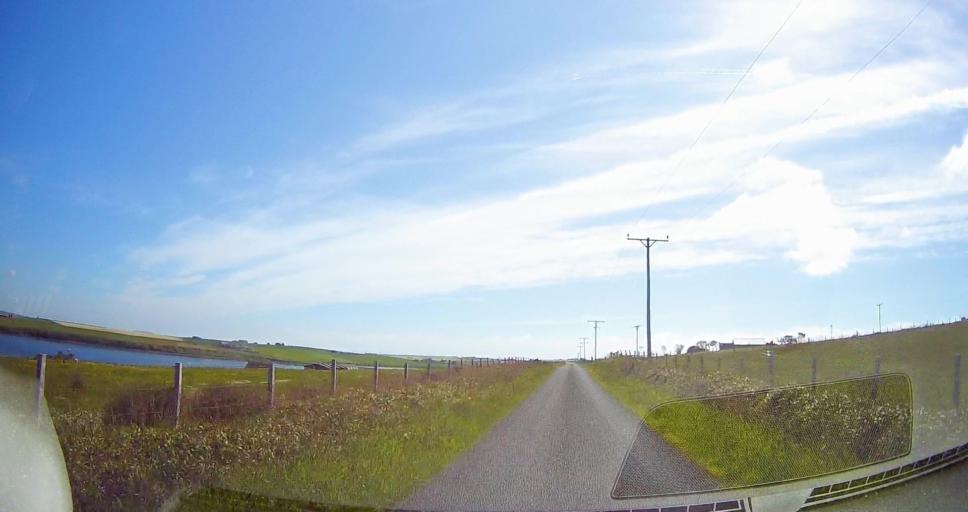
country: GB
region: Scotland
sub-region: Orkney Islands
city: Kirkwall
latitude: 58.8563
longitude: -2.9334
